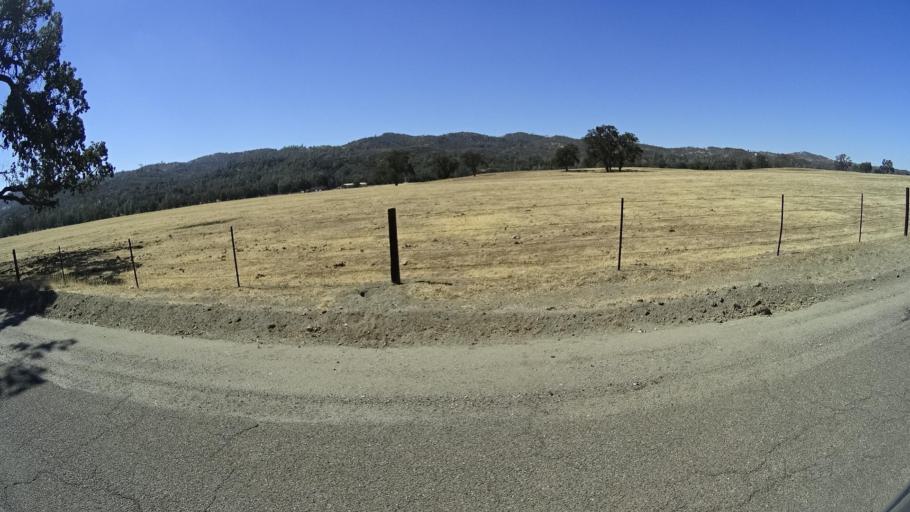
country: US
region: California
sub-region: Fresno County
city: Coalinga
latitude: 35.9389
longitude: -120.5181
